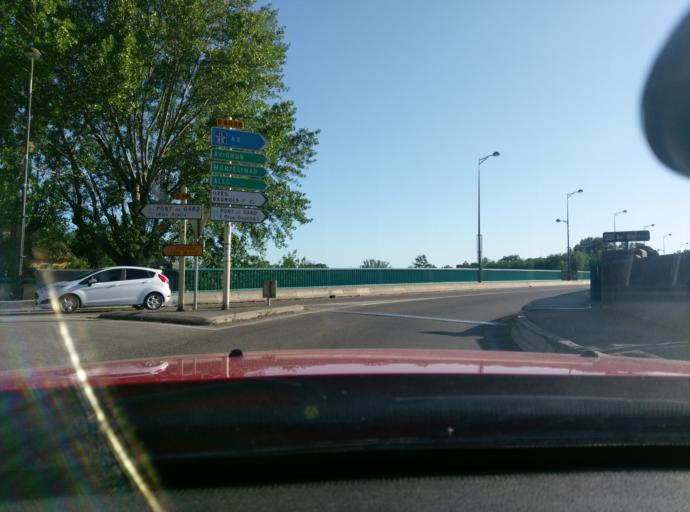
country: FR
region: Languedoc-Roussillon
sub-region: Departement du Gard
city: Remoulins
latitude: 43.9368
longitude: 4.5562
